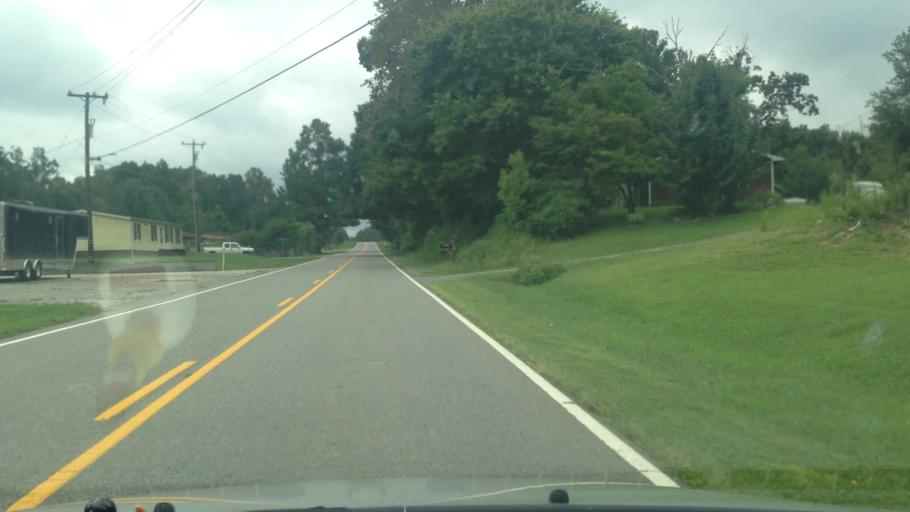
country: US
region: North Carolina
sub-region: Stokes County
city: Walnut Cove
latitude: 36.2686
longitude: -80.1454
